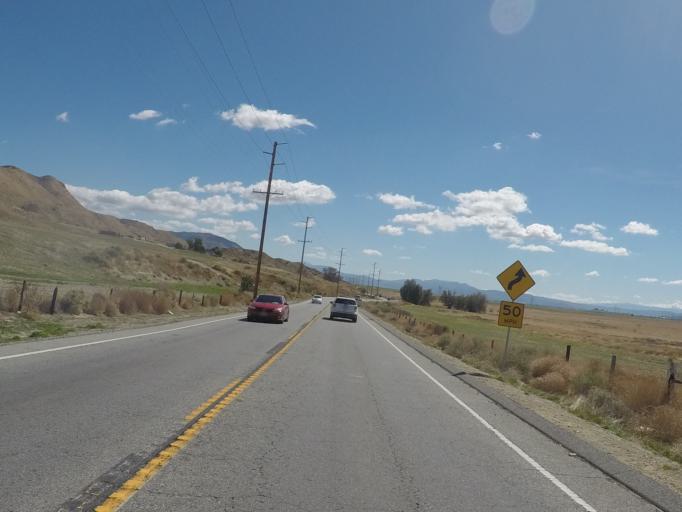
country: US
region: California
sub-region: Riverside County
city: Lakeview
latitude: 33.8816
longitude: -117.0591
